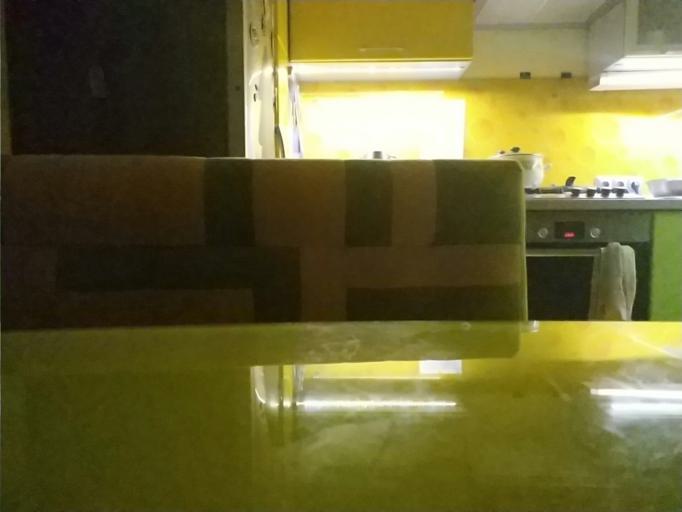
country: RU
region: Republic of Karelia
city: Pyaozerskiy
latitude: 65.9459
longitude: 30.4063
